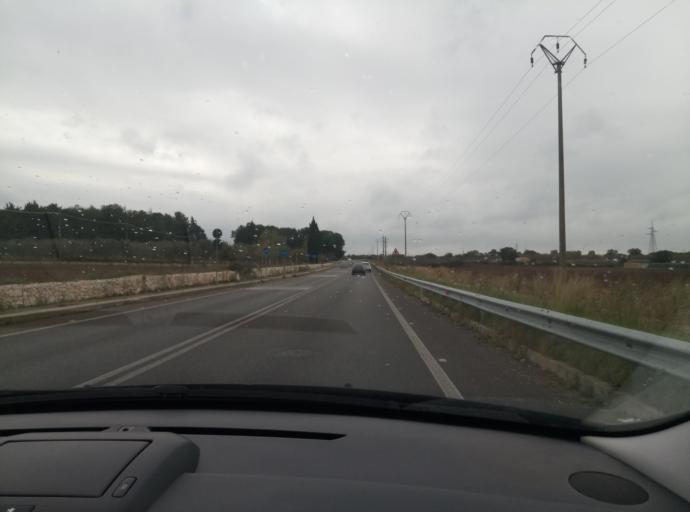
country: IT
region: Apulia
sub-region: Provincia di Bari
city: Acquaviva delle Fonti
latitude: 40.8818
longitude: 16.8118
